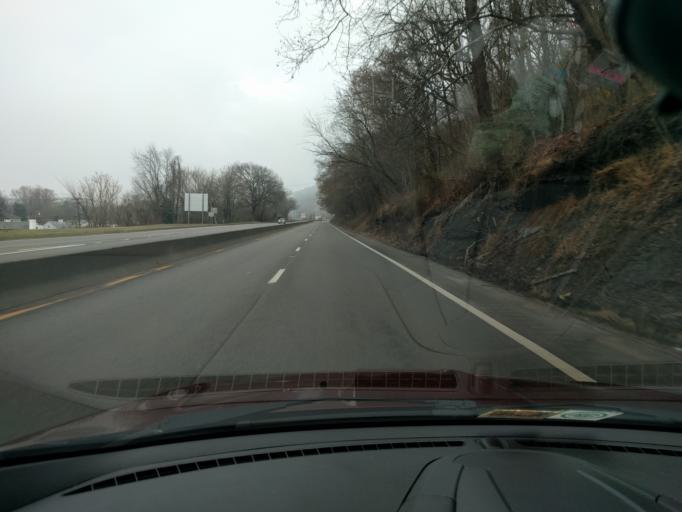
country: US
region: West Virginia
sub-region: Kanawha County
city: Rand
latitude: 38.3018
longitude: -81.5558
